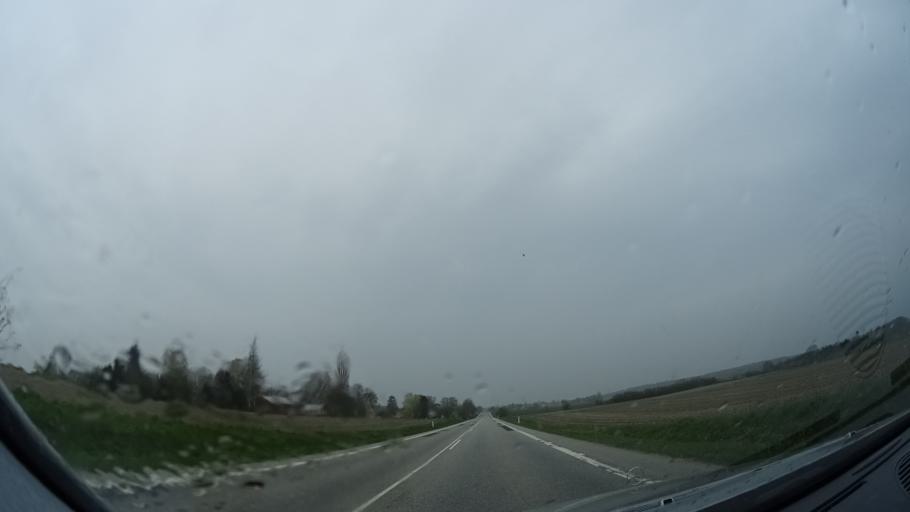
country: DK
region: Zealand
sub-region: Holbaek Kommune
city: Vipperod
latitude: 55.6938
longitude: 11.7864
